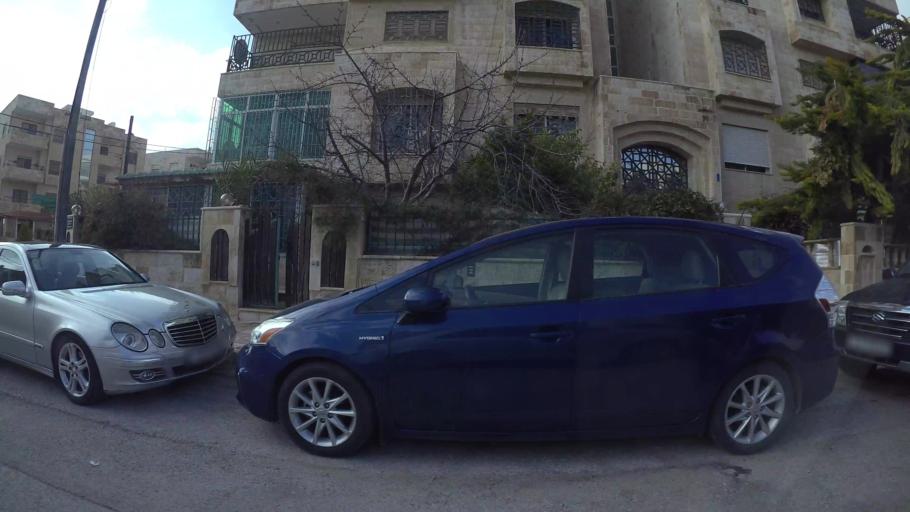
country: JO
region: Amman
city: Al Jubayhah
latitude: 31.9841
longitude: 35.8500
